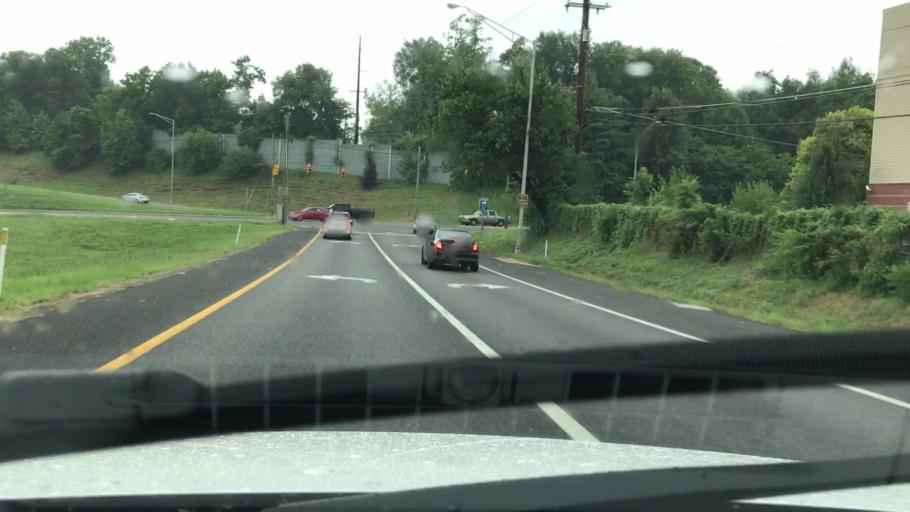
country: US
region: Tennessee
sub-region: Davidson County
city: Nashville
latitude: 36.1350
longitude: -86.7762
